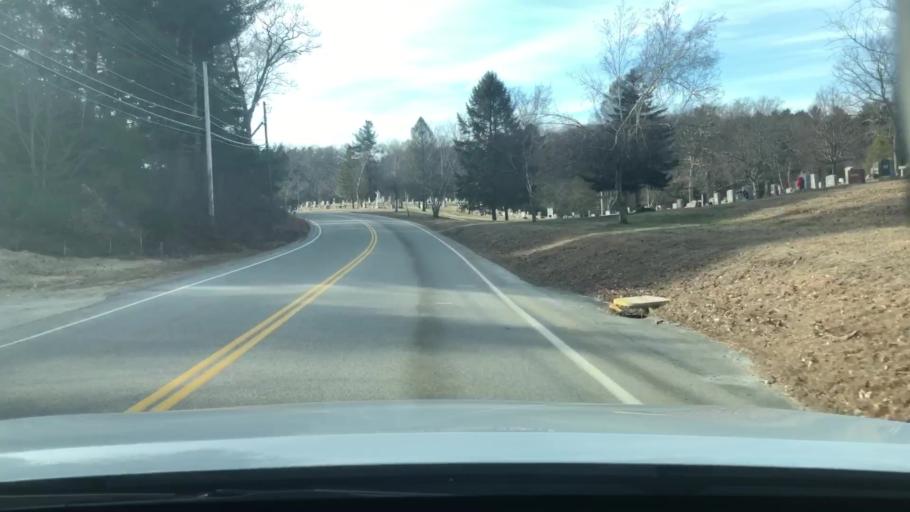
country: US
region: Massachusetts
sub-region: Worcester County
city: Grafton
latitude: 42.2038
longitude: -71.6999
